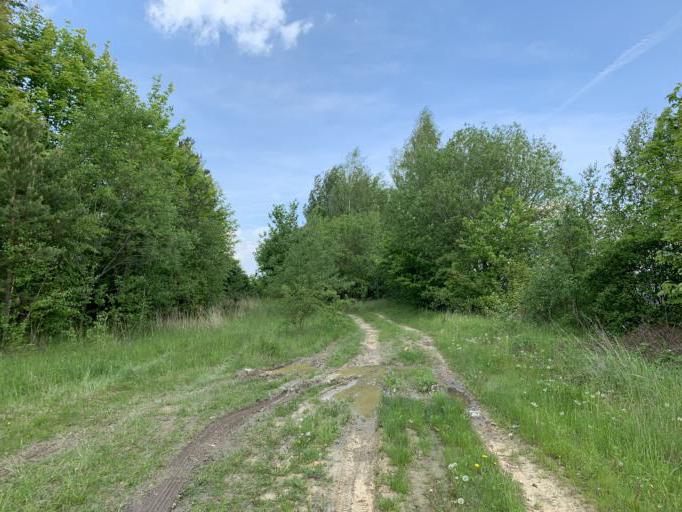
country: PL
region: Lower Silesian Voivodeship
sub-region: Powiat klodzki
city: Bystrzyca Klodzka
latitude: 50.3619
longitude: 16.6694
